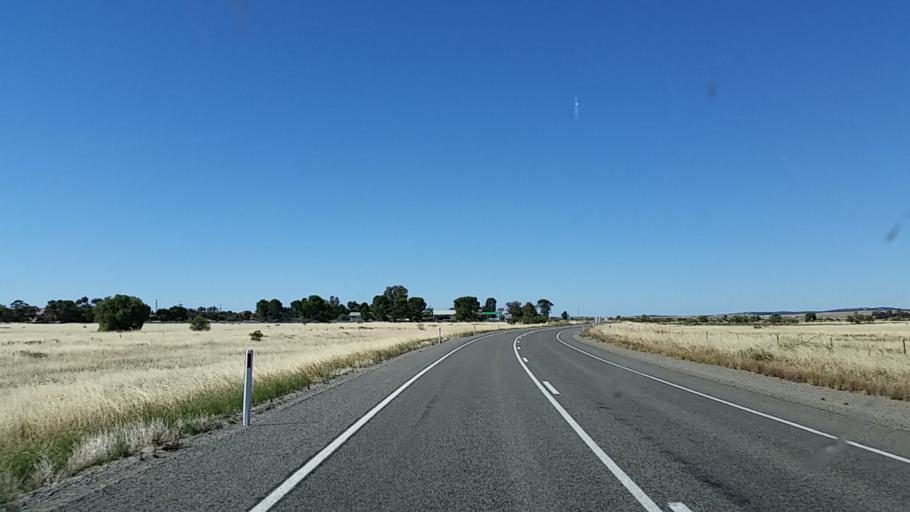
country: AU
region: South Australia
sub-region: Peterborough
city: Peterborough
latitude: -33.1567
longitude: 138.9200
